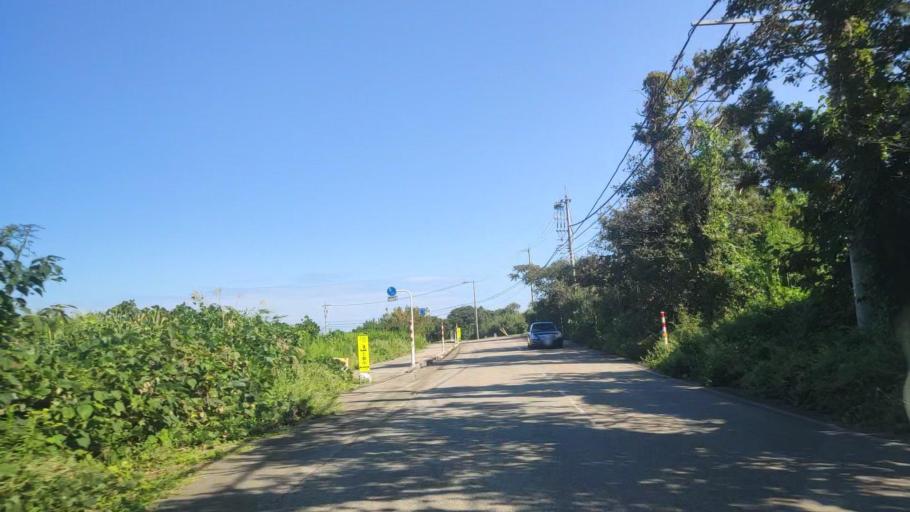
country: JP
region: Ishikawa
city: Hakui
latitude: 37.0715
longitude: 136.7214
